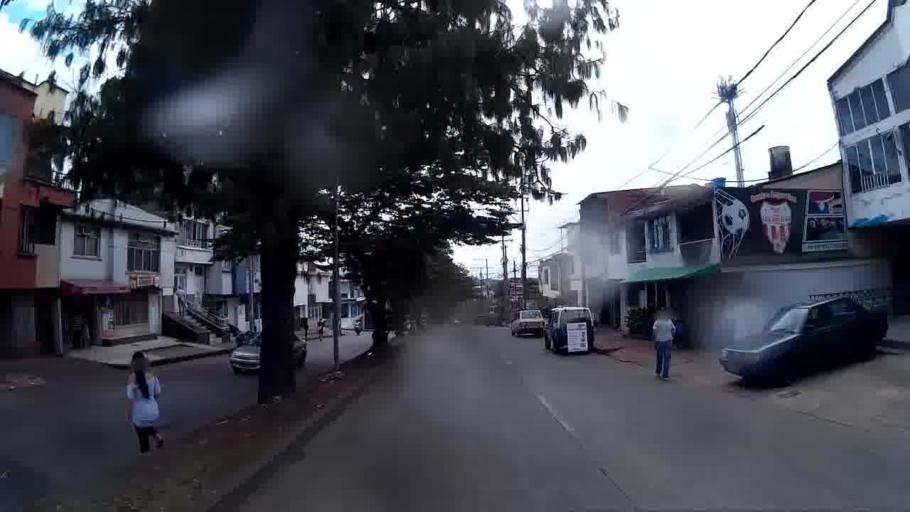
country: CO
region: Quindio
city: Armenia
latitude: 4.5432
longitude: -75.6641
